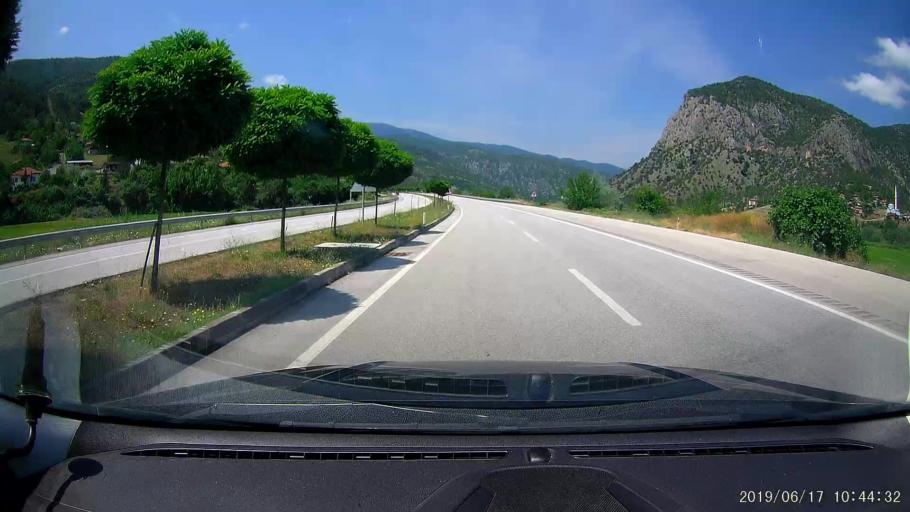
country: TR
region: Corum
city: Hacihamza
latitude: 41.0711
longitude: 34.5096
